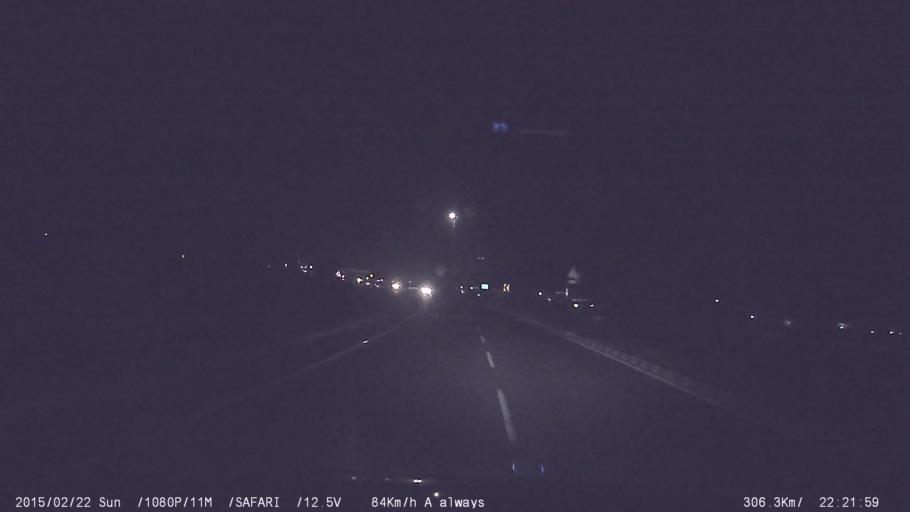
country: IN
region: Tamil Nadu
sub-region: Karur
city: Karur
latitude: 11.0098
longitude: 78.0688
